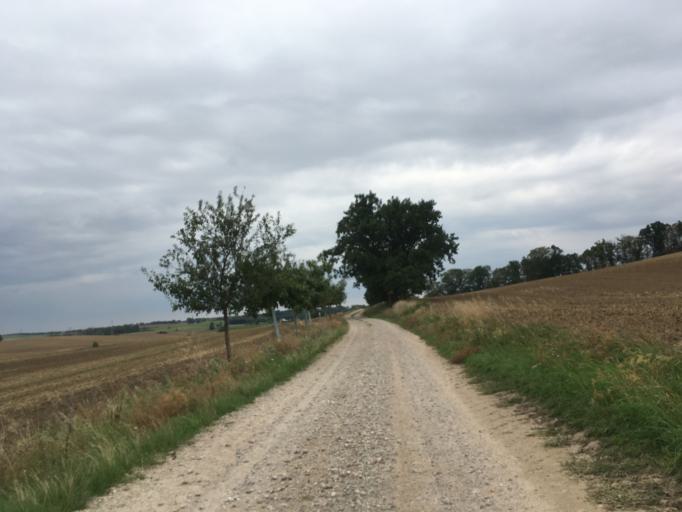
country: DE
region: Brandenburg
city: Angermunde
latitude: 53.0649
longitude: 14.0194
